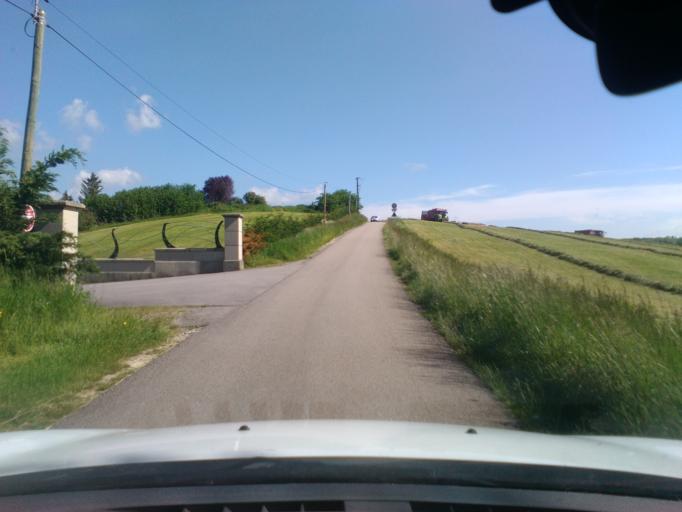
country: FR
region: Lorraine
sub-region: Departement des Vosges
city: Mirecourt
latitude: 48.3271
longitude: 6.1454
